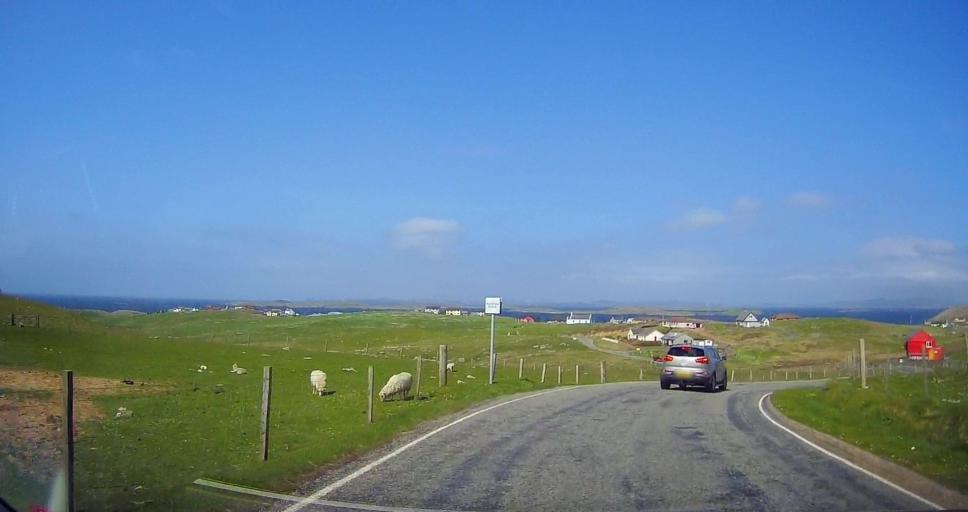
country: GB
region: Scotland
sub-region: Shetland Islands
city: Sandwick
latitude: 60.1001
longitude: -1.3217
